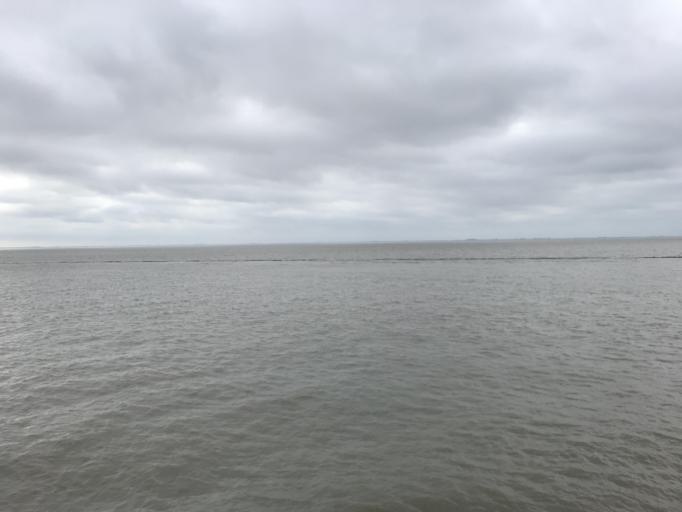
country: DE
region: Lower Saxony
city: Emden
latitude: 53.3303
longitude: 7.1151
